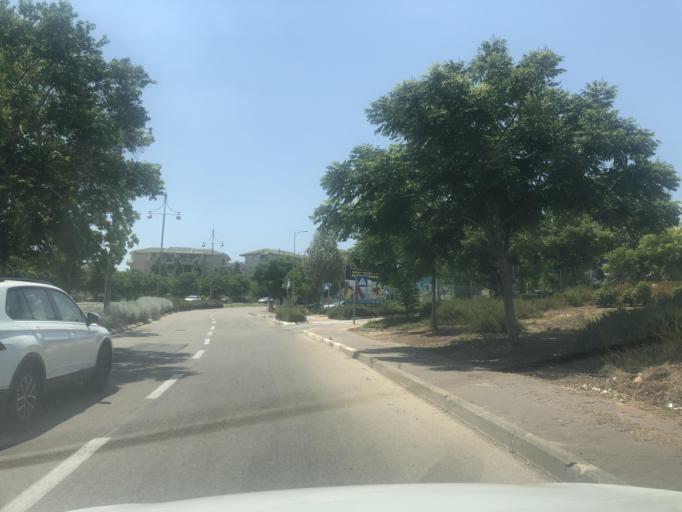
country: IL
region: Haifa
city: Daliyat el Karmil
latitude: 32.6460
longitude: 35.0940
